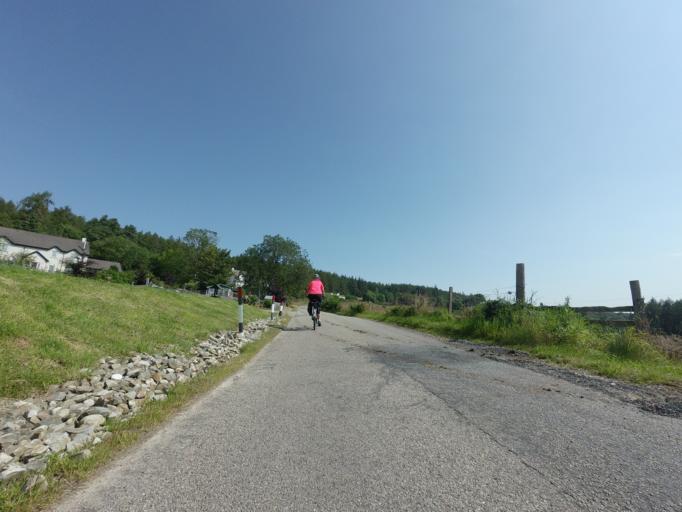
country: GB
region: Scotland
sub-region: Highland
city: Invergordon
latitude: 57.7569
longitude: -4.1337
